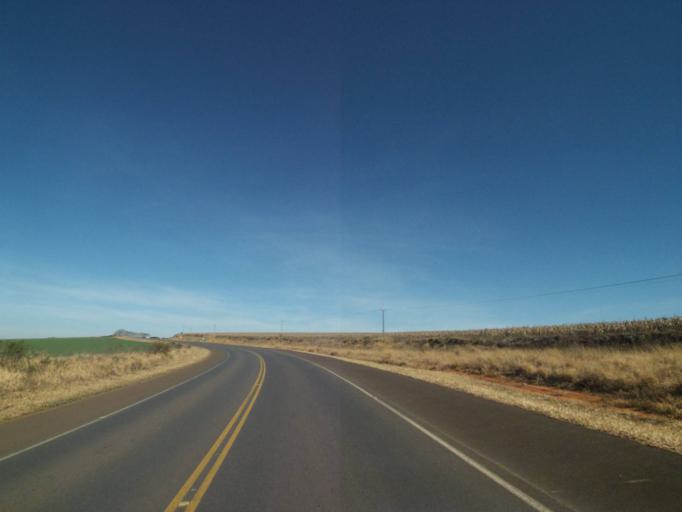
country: BR
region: Parana
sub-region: Tibagi
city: Tibagi
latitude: -24.3916
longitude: -50.3363
